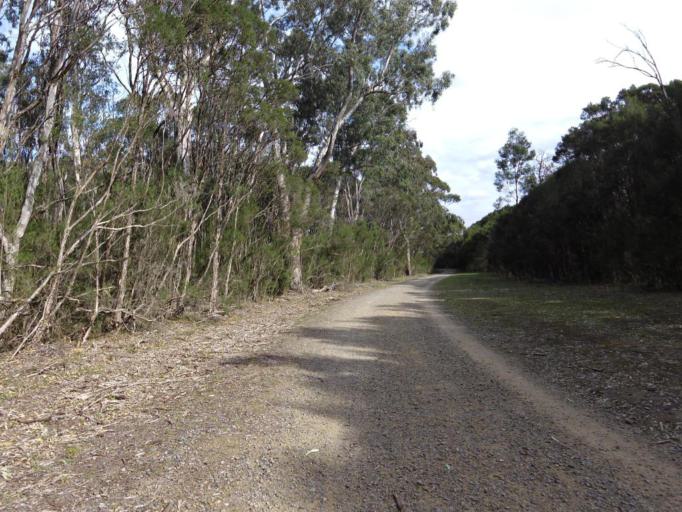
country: AU
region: Victoria
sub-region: Yarra Ranges
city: Lysterfield
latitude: -37.9520
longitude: 145.2974
